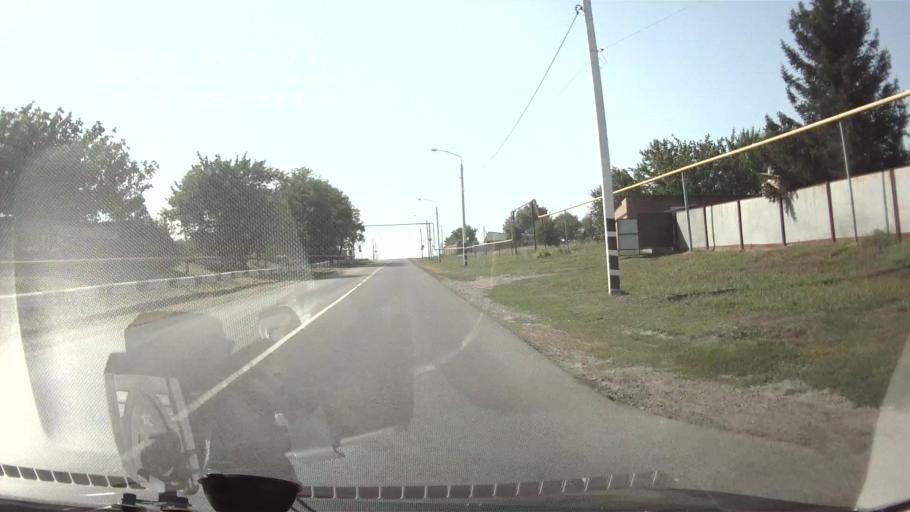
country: RU
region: Krasnodarskiy
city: Novopokrovskaya
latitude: 45.9340
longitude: 40.7120
